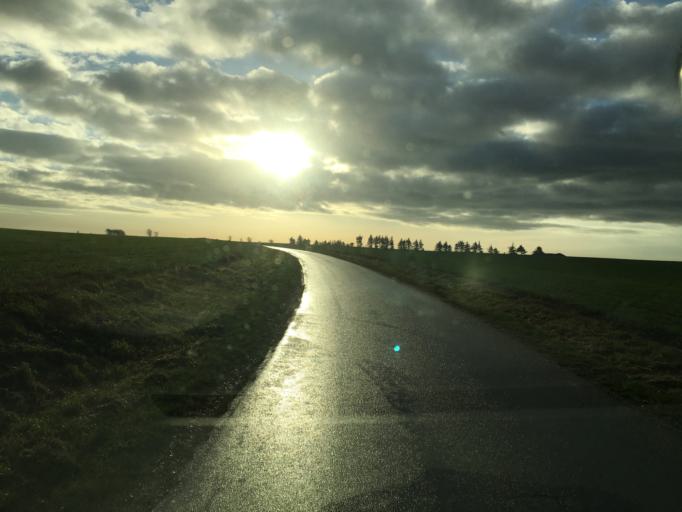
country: DK
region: South Denmark
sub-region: Tonder Kommune
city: Sherrebek
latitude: 55.1652
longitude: 8.8111
